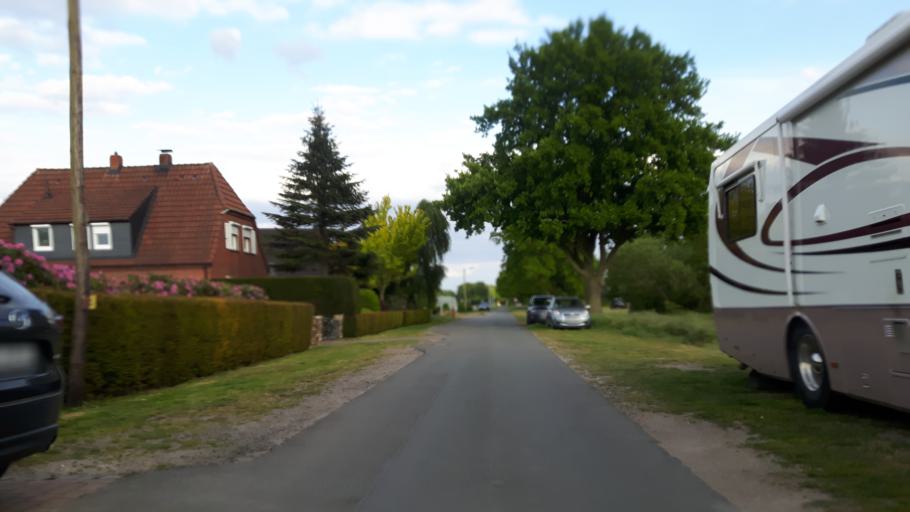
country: DE
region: Lower Saxony
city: Gross Ippener
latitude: 53.0121
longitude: 8.5984
